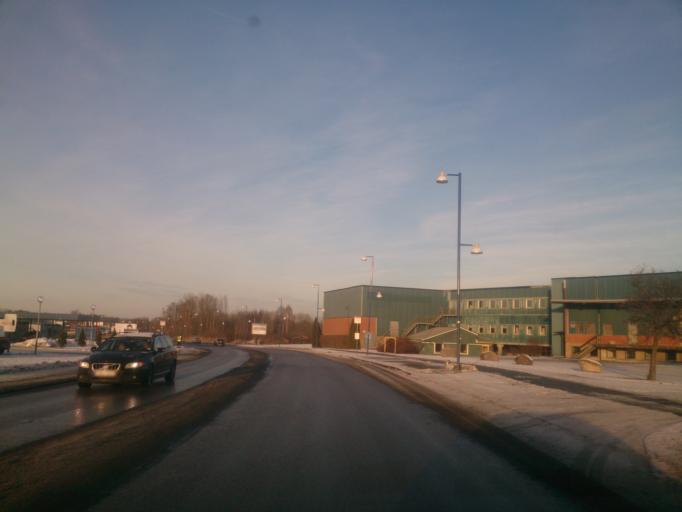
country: SE
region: OEstergoetland
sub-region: Norrkopings Kommun
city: Norrkoping
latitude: 58.6094
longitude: 16.1791
